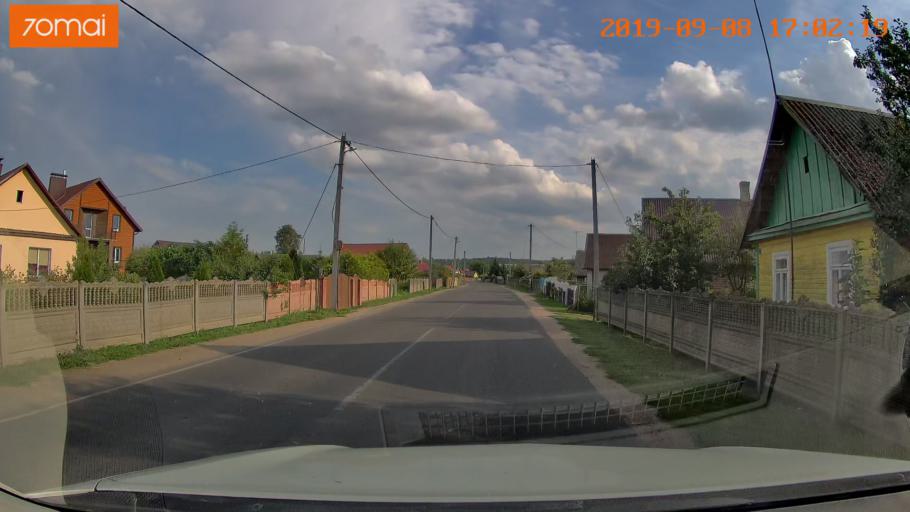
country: BY
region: Grodnenskaya
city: Hrodna
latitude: 53.7045
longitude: 23.9384
